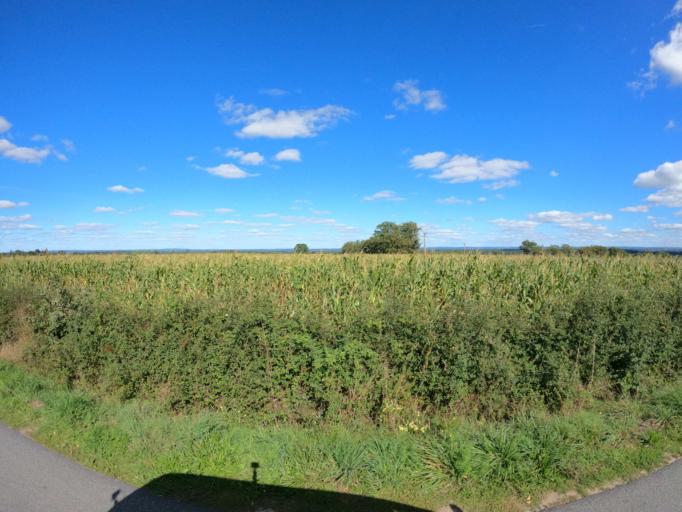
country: FR
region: Auvergne
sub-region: Departement de l'Allier
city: Doyet
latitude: 46.4040
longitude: 2.7417
